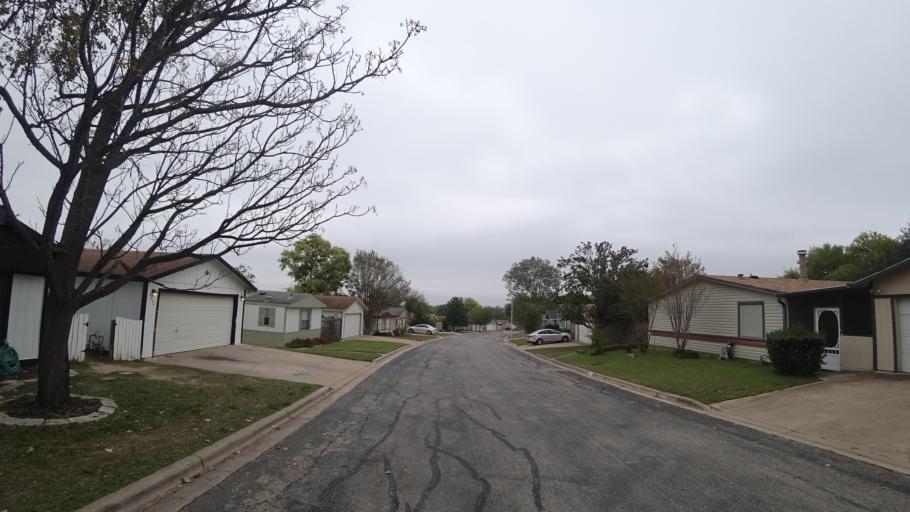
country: US
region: Texas
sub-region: Travis County
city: Pflugerville
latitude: 30.3926
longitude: -97.6411
